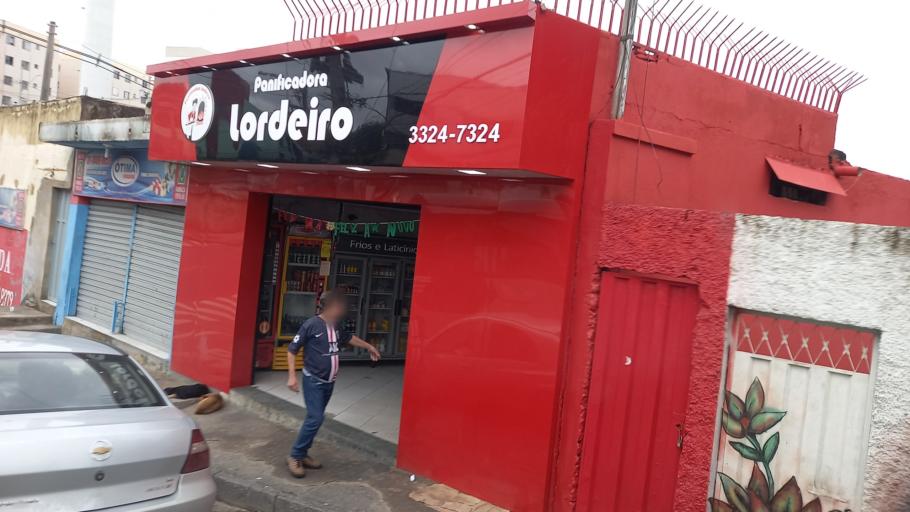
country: BR
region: Minas Gerais
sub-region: Belo Horizonte
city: Belo Horizonte
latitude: -19.9171
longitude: -43.8886
